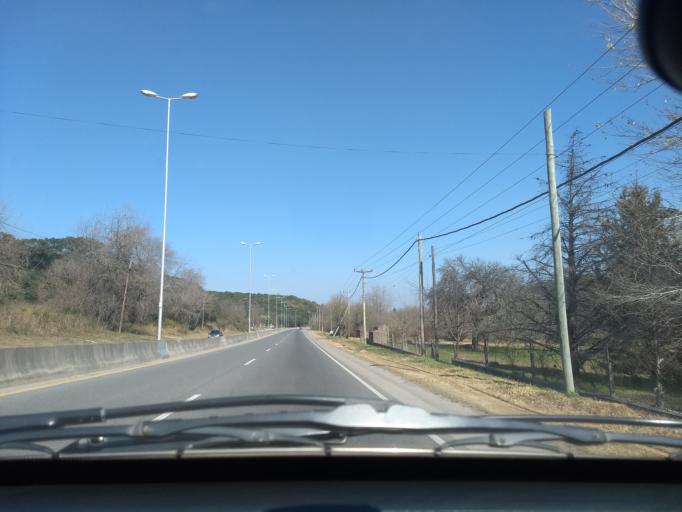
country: AR
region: Cordoba
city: Rio Ceballos
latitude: -31.1646
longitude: -64.3017
